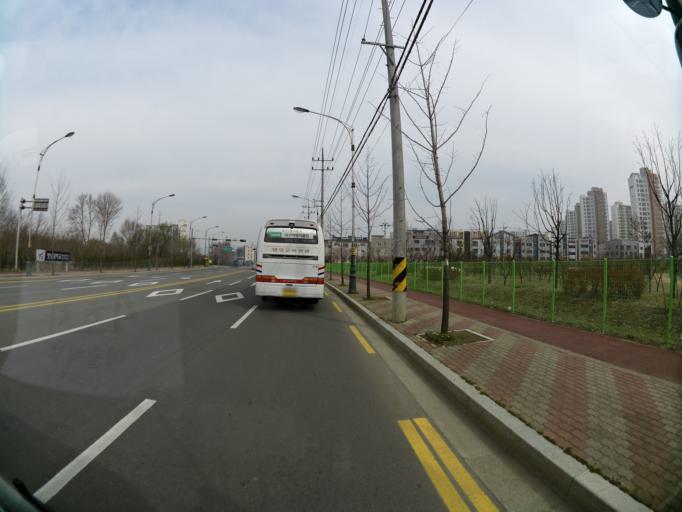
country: KR
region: Gyeongsangbuk-do
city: Gyeongsan-si
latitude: 35.8367
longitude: 128.7649
